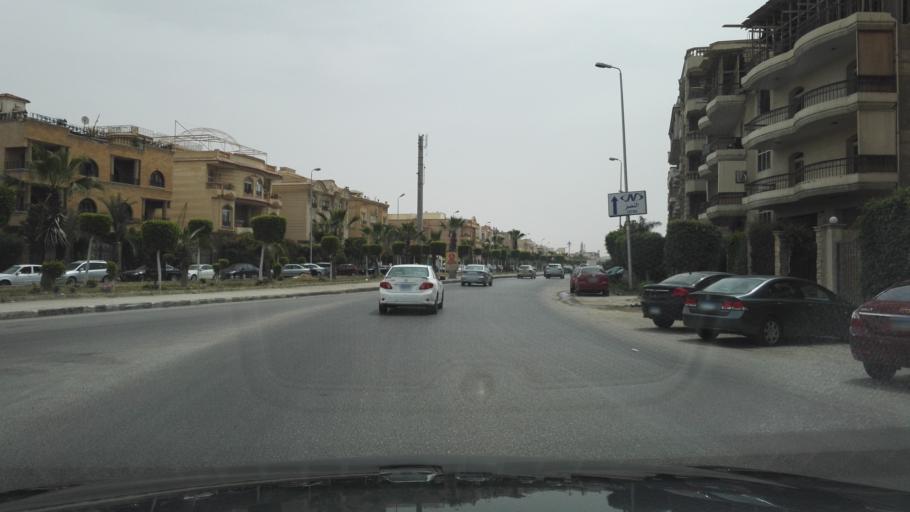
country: EG
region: Muhafazat al Qahirah
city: Cairo
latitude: 30.0072
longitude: 31.4122
